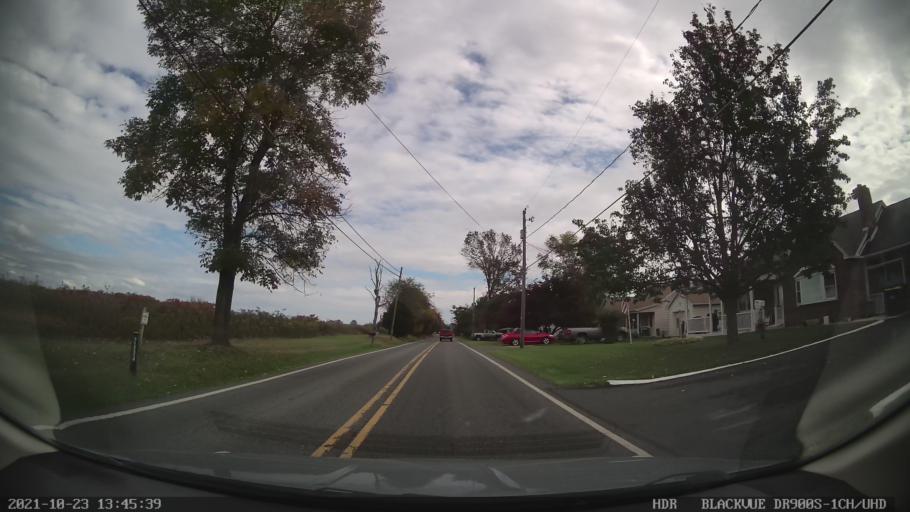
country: US
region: Pennsylvania
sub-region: Montgomery County
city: Pennsburg
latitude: 40.3799
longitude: -75.5247
